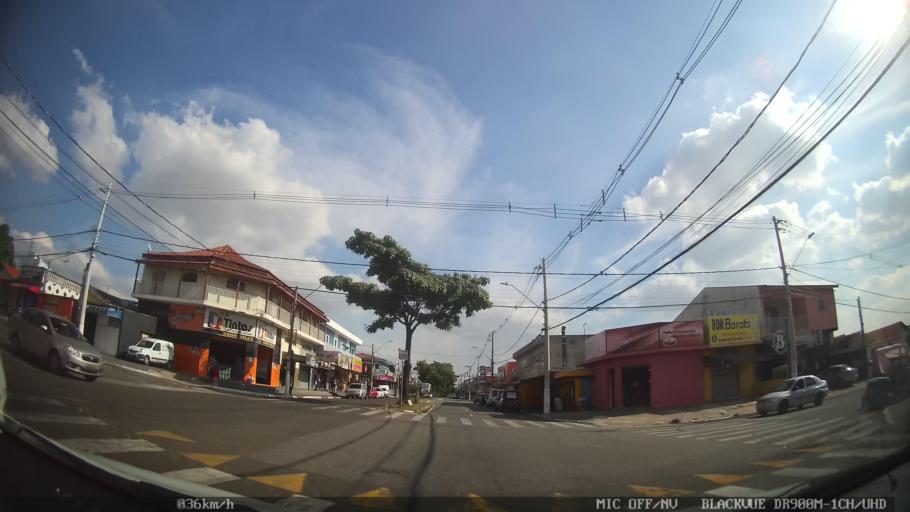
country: BR
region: Sao Paulo
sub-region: Hortolandia
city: Hortolandia
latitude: -22.9036
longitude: -47.2440
